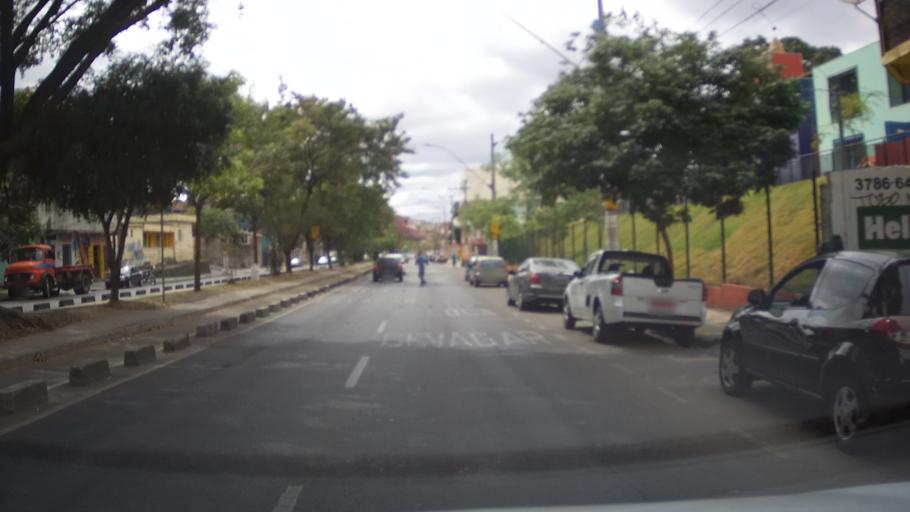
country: BR
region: Minas Gerais
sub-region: Belo Horizonte
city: Belo Horizonte
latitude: -19.8409
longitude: -43.9239
